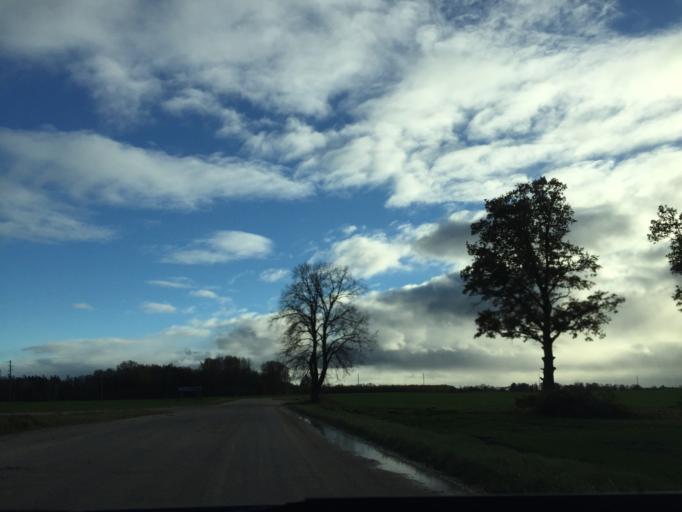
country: LV
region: Tukuma Rajons
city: Tukums
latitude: 56.9353
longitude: 22.9532
